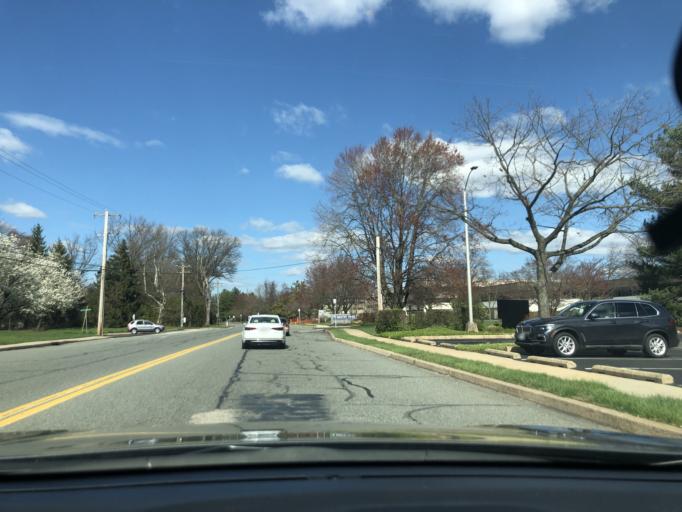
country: US
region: Pennsylvania
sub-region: Montgomery County
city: Blue Bell
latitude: 40.1334
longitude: -75.2764
